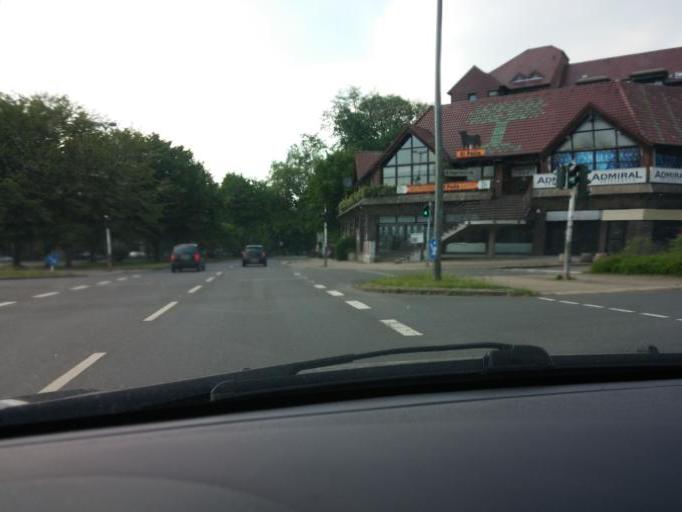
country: DE
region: North Rhine-Westphalia
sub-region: Regierungsbezirk Munster
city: Gladbeck
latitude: 51.5818
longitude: 7.0529
